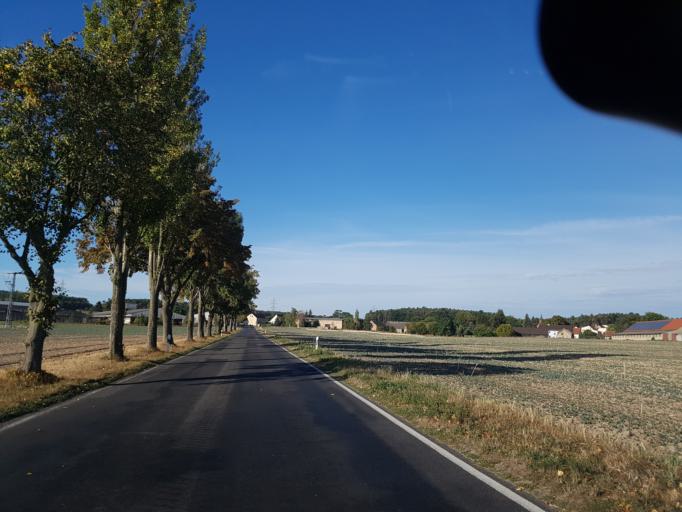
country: DE
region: Brandenburg
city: Belzig
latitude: 52.0999
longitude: 12.6235
